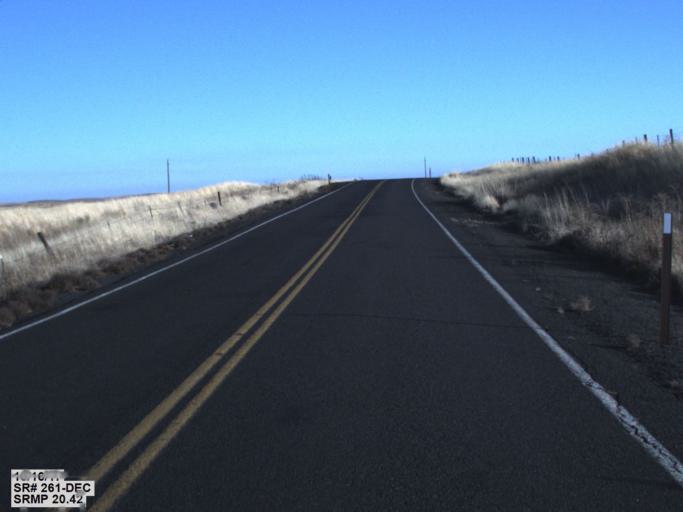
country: US
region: Washington
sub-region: Walla Walla County
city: Waitsburg
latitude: 46.6546
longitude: -118.2609
